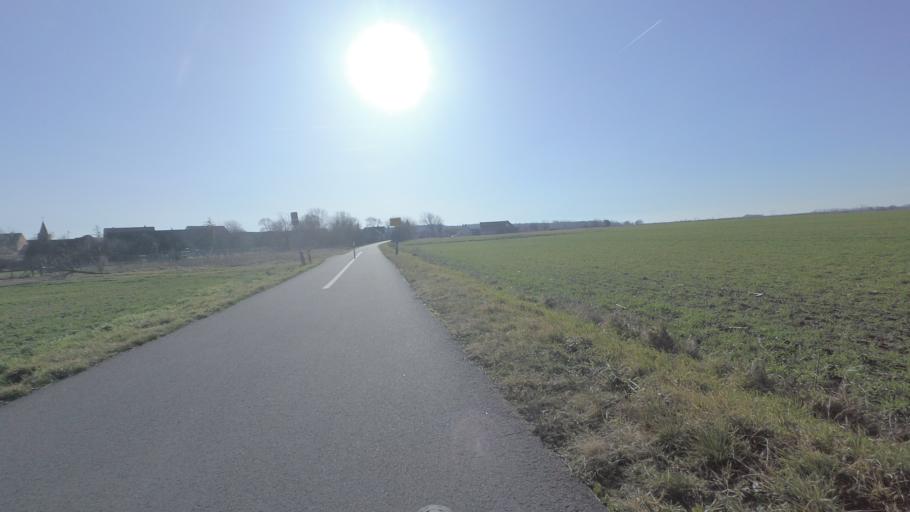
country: DE
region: Brandenburg
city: Luckenwalde
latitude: 52.0418
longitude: 13.1357
